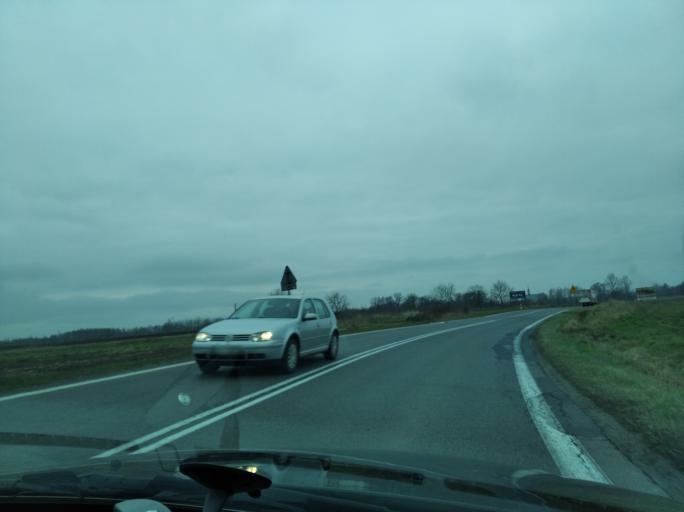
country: PL
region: Subcarpathian Voivodeship
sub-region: Powiat lancucki
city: Zolynia
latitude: 50.1744
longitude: 22.3139
